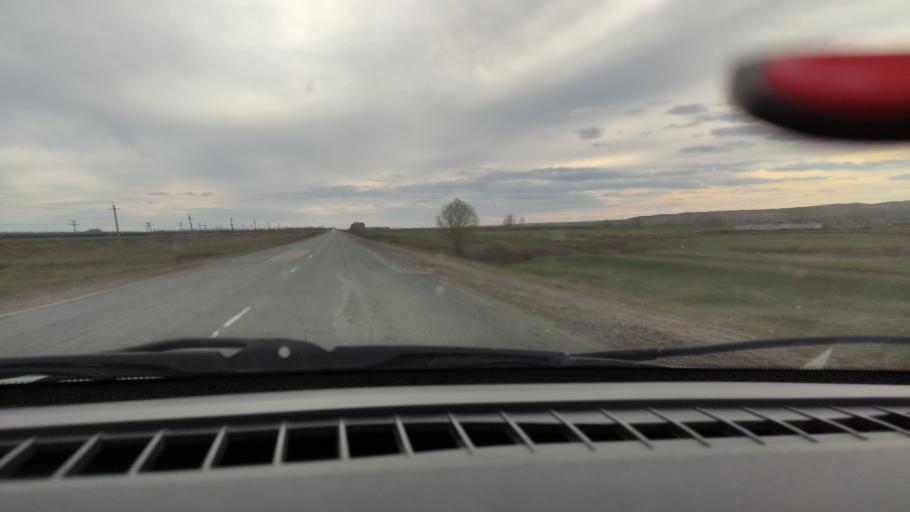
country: RU
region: Bashkortostan
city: Mayachnyy
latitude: 52.4170
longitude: 55.7653
